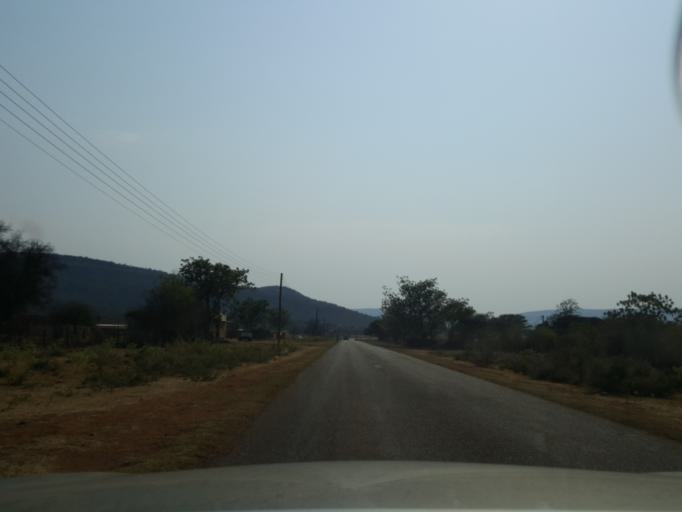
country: BW
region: South East
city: Lobatse
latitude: -25.3085
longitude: 25.8125
